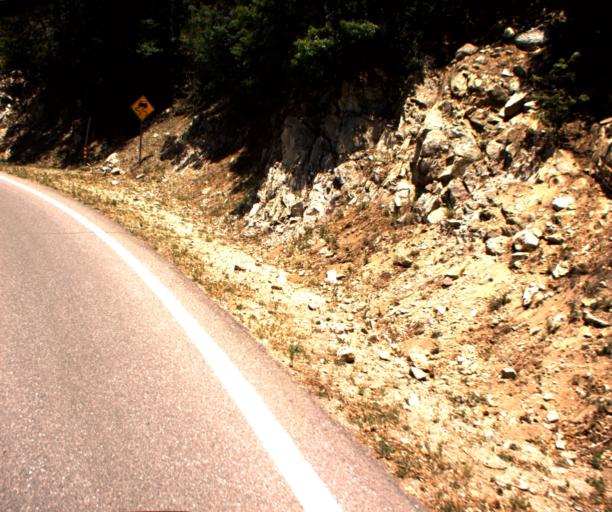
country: US
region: Arizona
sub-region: Graham County
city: Swift Trail Junction
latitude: 32.6284
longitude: -109.8369
